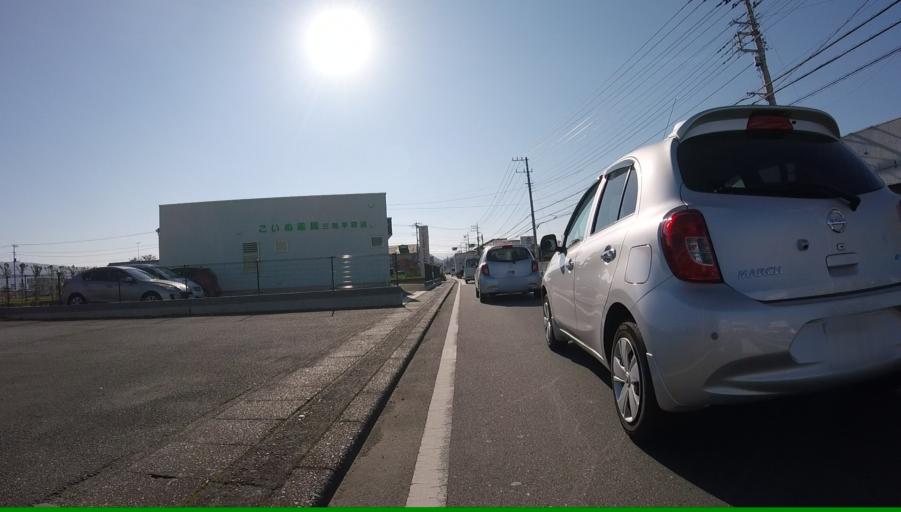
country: JP
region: Shizuoka
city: Mishima
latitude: 35.0984
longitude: 138.9155
